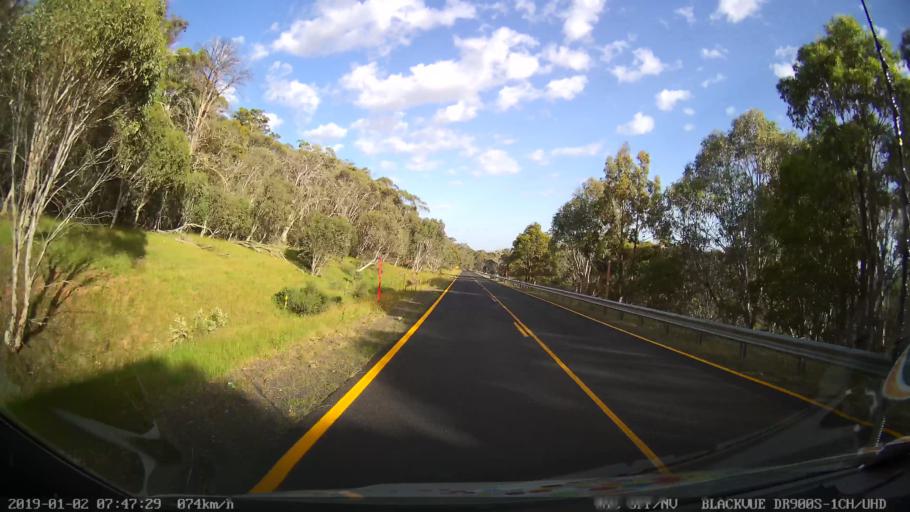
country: AU
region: New South Wales
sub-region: Tumut Shire
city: Tumut
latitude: -35.7643
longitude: 148.5204
